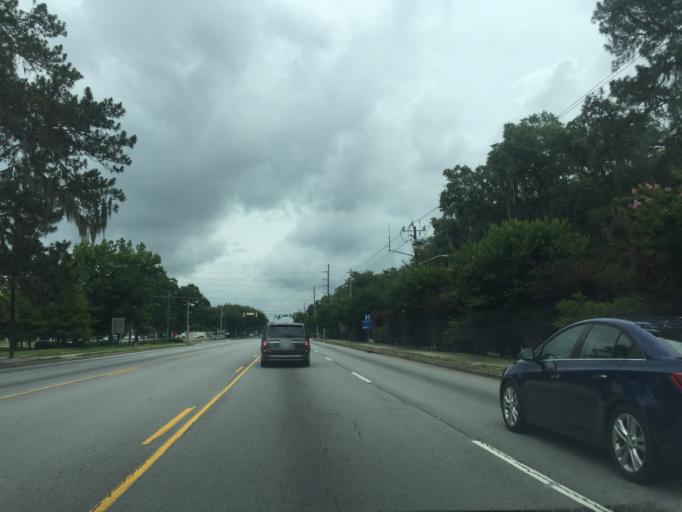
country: US
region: Georgia
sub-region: Chatham County
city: Thunderbolt
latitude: 32.0270
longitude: -81.1036
